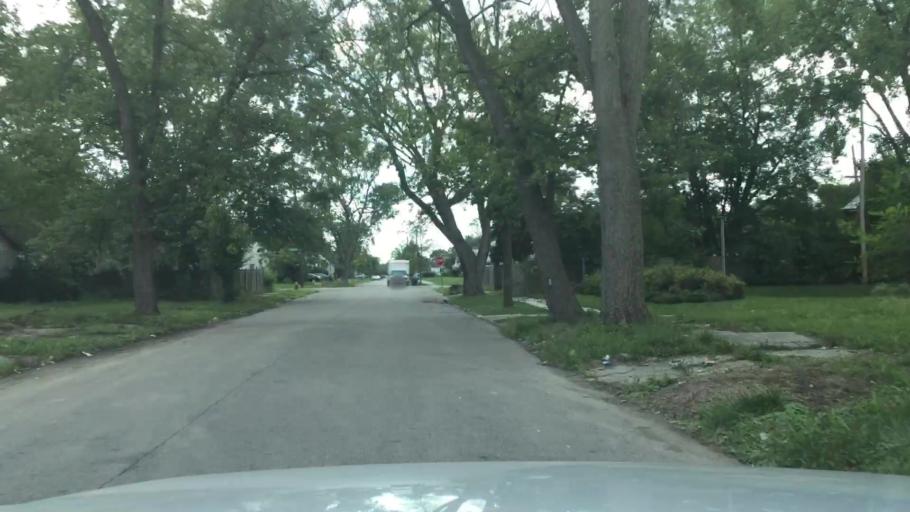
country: US
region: Michigan
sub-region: Wayne County
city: Dearborn Heights
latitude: 42.3514
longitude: -83.2223
